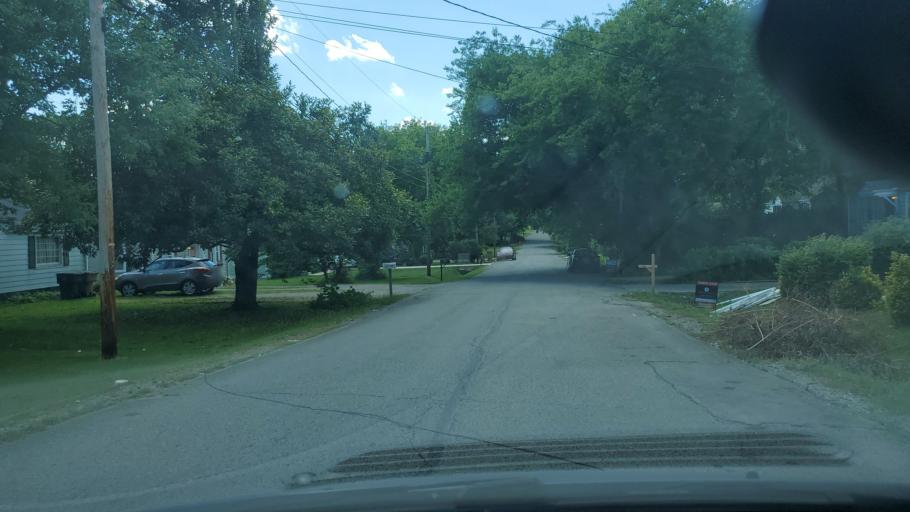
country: US
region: Tennessee
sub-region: Davidson County
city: Nashville
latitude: 36.1993
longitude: -86.7547
